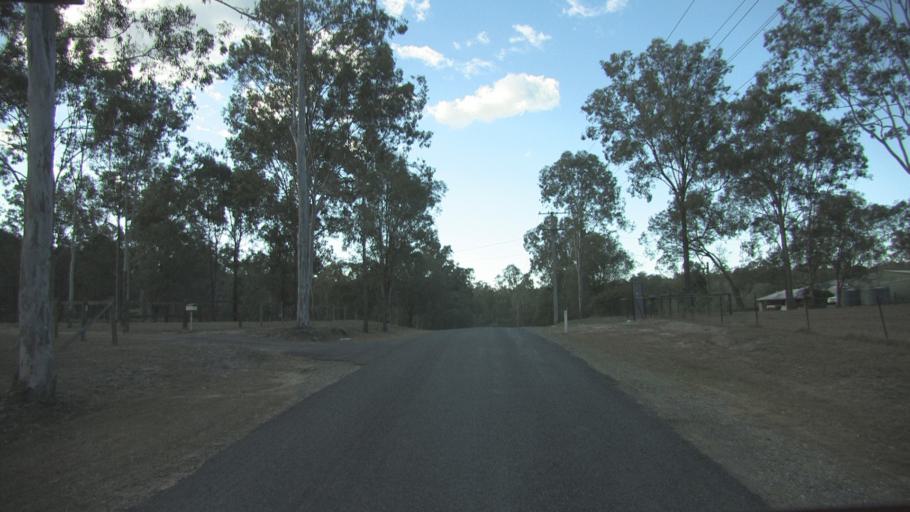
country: AU
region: Queensland
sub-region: Logan
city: Cedar Vale
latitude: -27.8480
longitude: 153.0908
